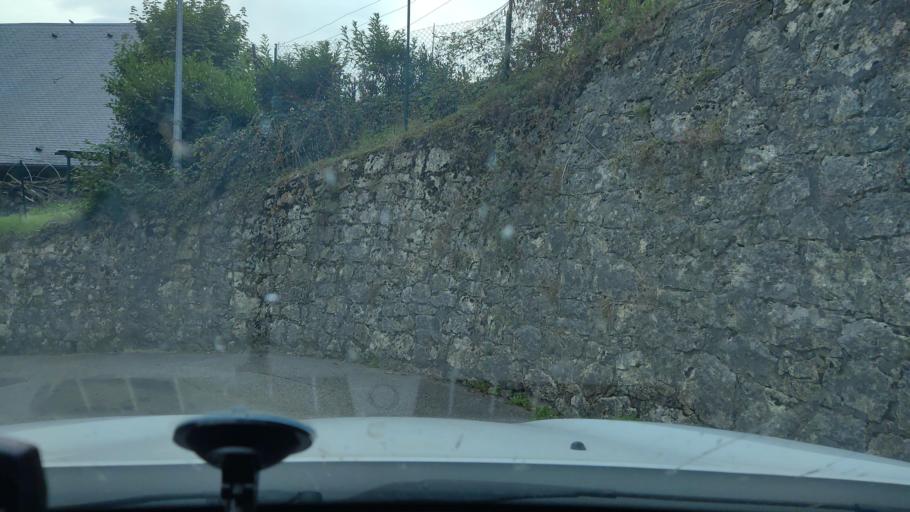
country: FR
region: Rhone-Alpes
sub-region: Departement de la Savoie
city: Voglans
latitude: 45.6292
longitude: 5.9085
